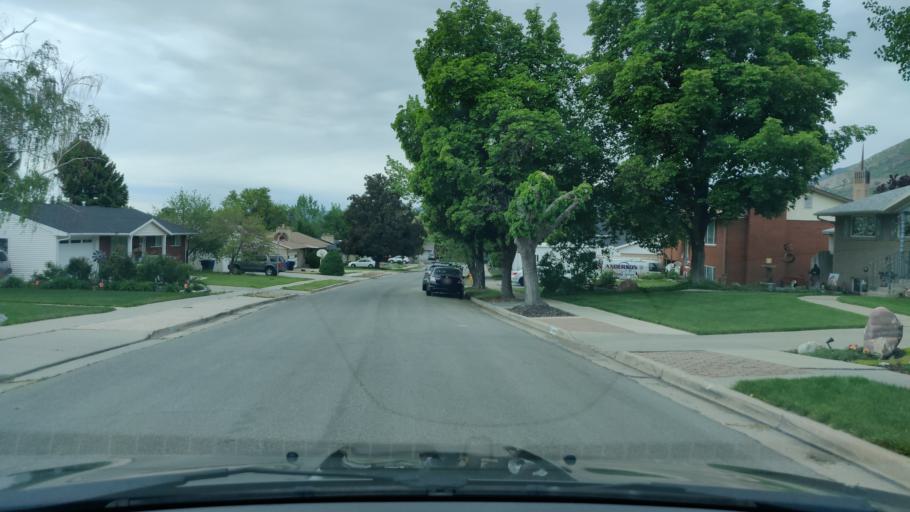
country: US
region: Utah
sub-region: Salt Lake County
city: Cottonwood Heights
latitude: 40.6277
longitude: -111.8204
